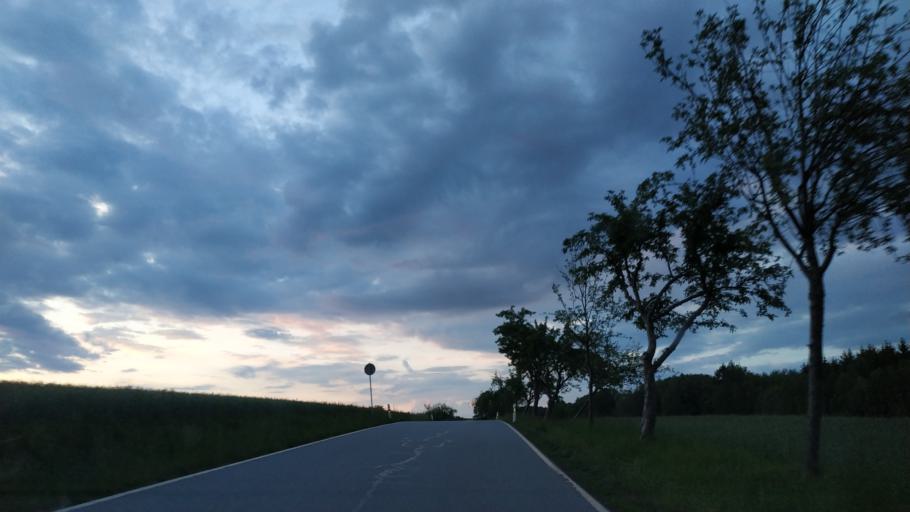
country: DE
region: Saxony
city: Hohnstein
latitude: 50.9764
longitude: 14.0918
